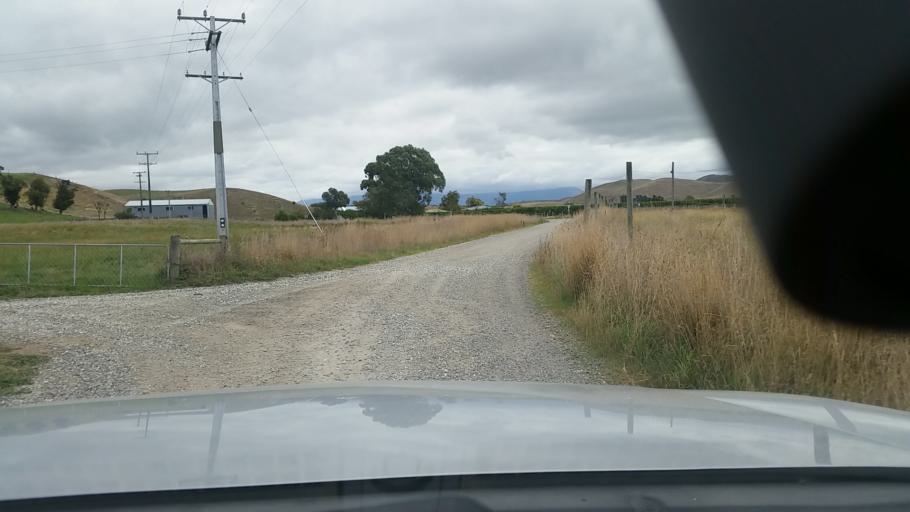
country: NZ
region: Marlborough
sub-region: Marlborough District
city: Blenheim
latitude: -41.7012
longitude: 174.1147
